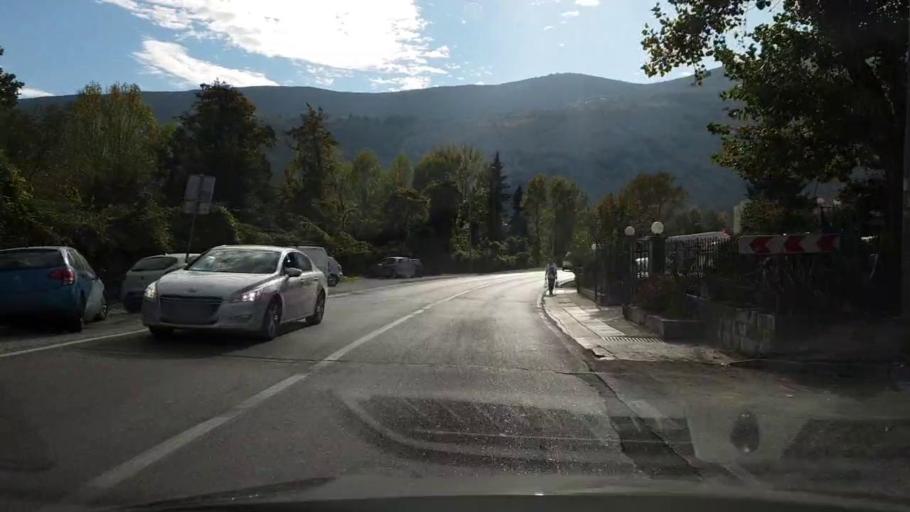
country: ME
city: Igalo
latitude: 42.4565
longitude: 18.5052
